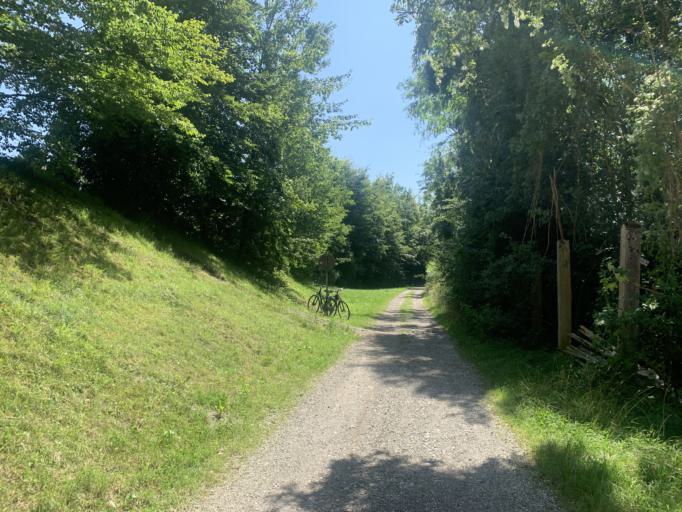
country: DE
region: Bavaria
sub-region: Upper Bavaria
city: Baierbrunn
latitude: 47.9961
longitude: 11.4850
